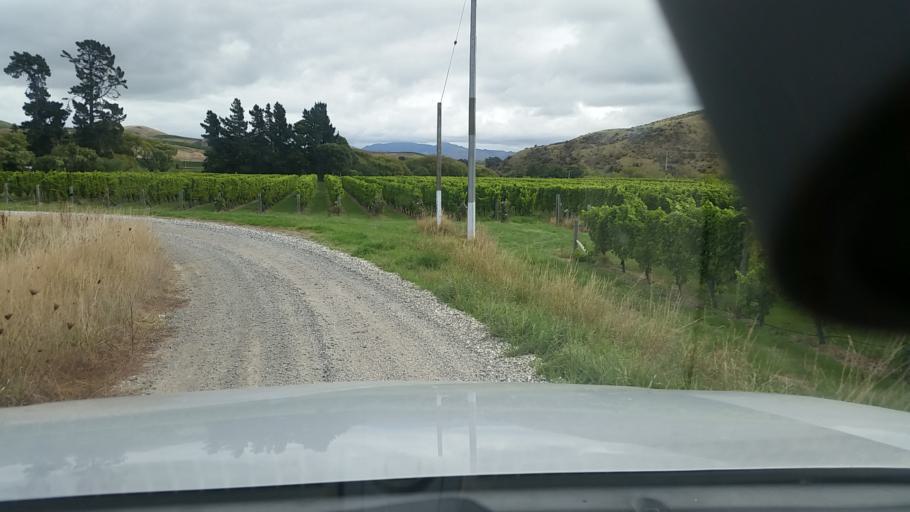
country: NZ
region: Marlborough
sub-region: Marlborough District
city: Blenheim
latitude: -41.6868
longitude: 174.1281
